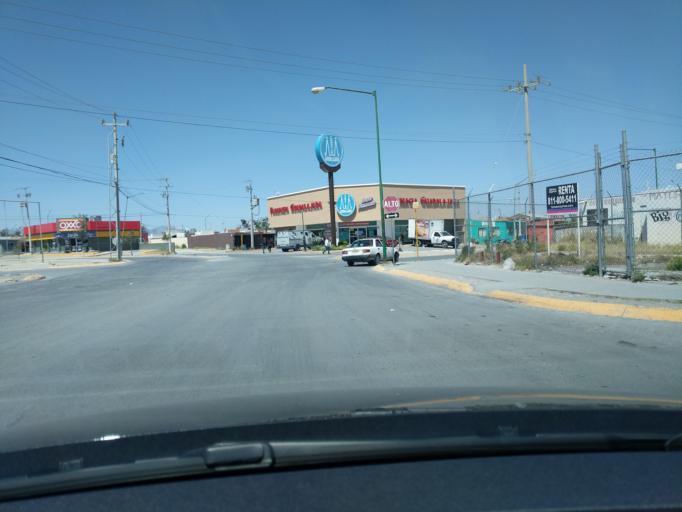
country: MX
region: Nuevo Leon
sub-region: Pesqueria
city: Colinas del Aeropuerto
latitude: 25.8260
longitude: -100.1166
